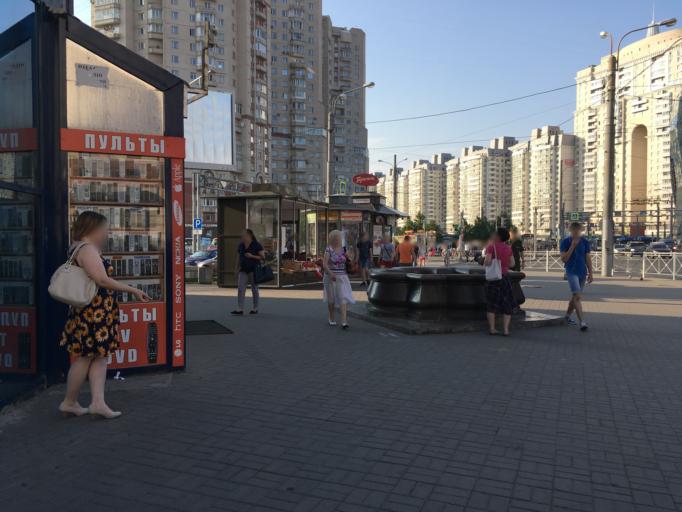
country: RU
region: St.-Petersburg
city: Komendantsky aerodrom
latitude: 60.0066
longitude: 30.2581
